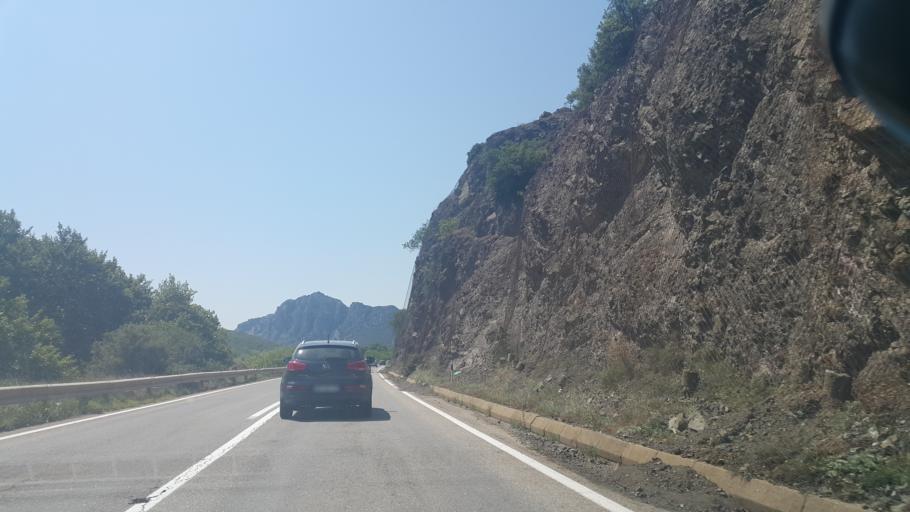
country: MK
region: Demir Kapija
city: Demir Kapija
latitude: 41.4053
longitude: 22.2959
